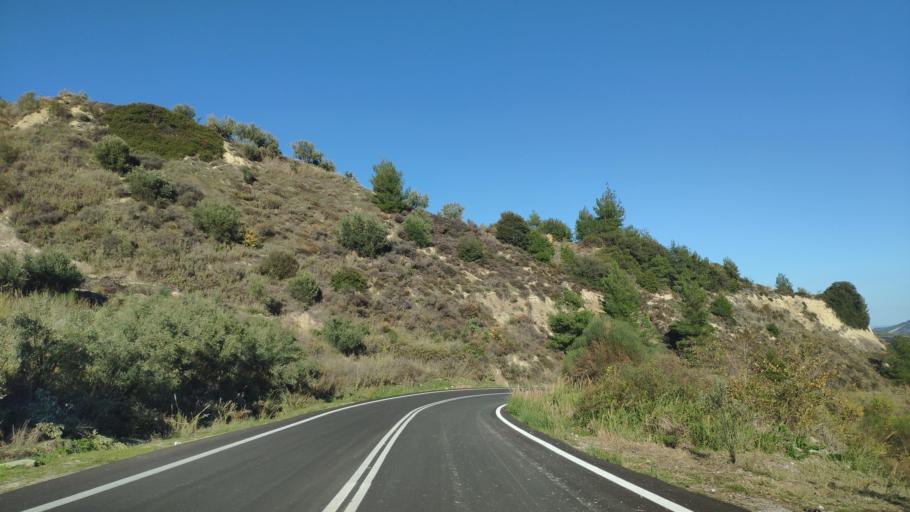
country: GR
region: Peloponnese
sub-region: Nomos Korinthias
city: Xylokastro
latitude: 38.0023
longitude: 22.5060
